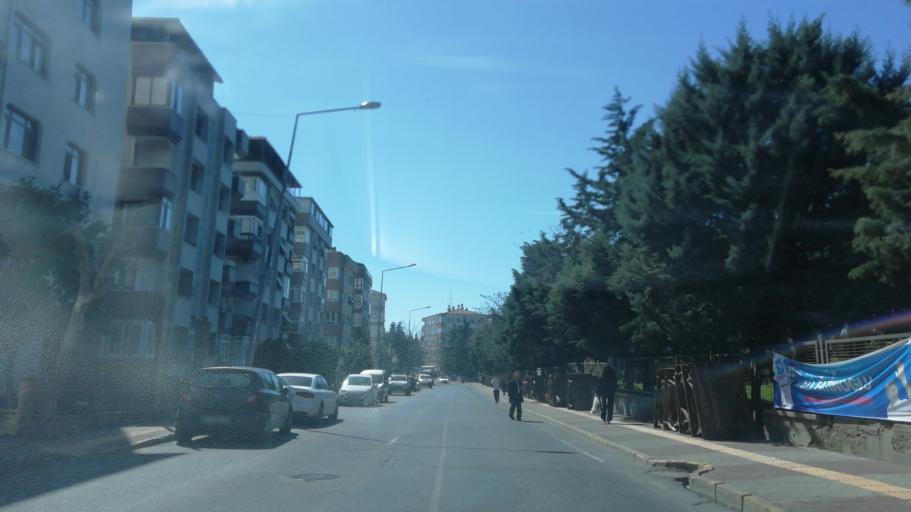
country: TR
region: Istanbul
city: Bahcelievler
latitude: 40.9893
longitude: 28.8664
